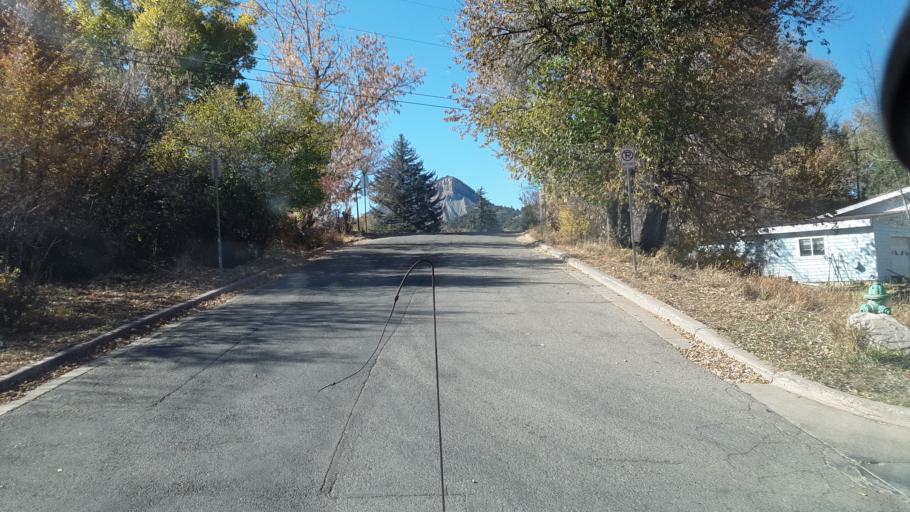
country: US
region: Colorado
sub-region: La Plata County
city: Durango
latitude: 37.2859
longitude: -107.8746
